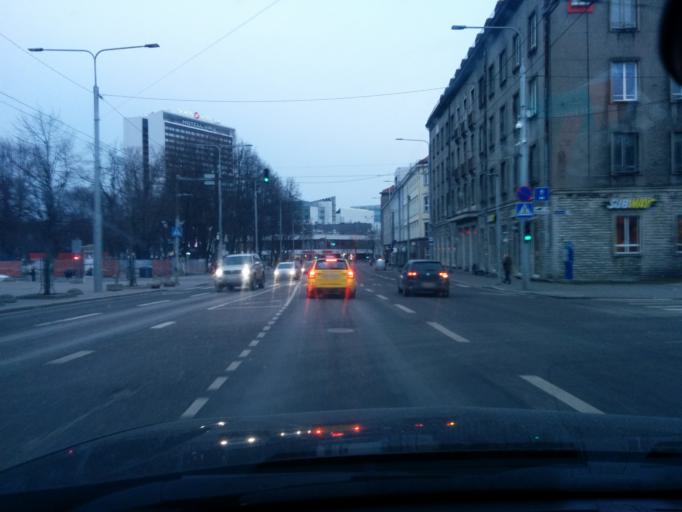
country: EE
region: Harju
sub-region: Tallinna linn
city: Tallinn
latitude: 59.4344
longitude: 24.7515
